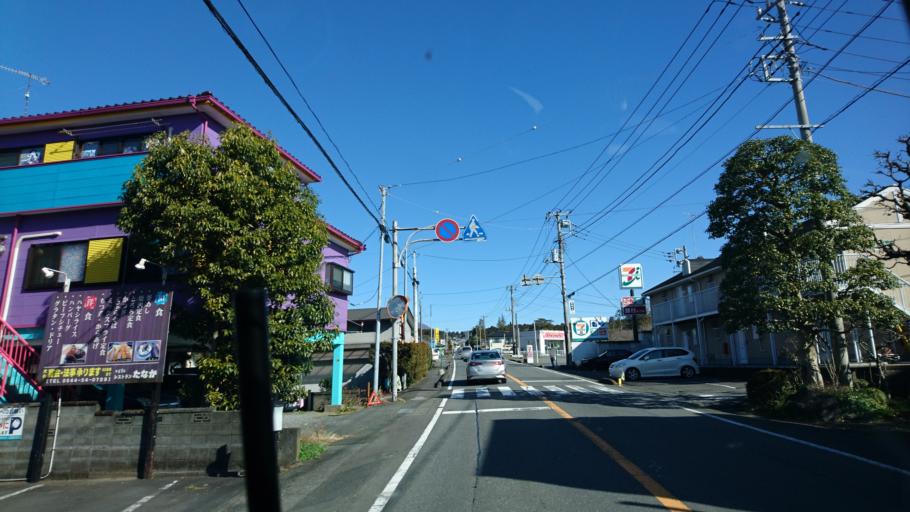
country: JP
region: Shizuoka
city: Fujinomiya
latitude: 35.3047
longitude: 138.5942
